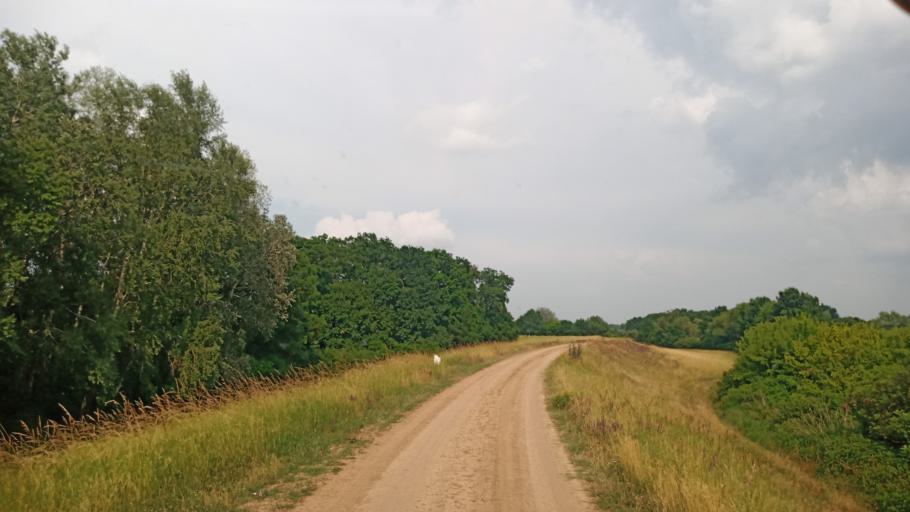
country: HU
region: Bekes
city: Doboz
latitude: 46.7065
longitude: 21.2881
